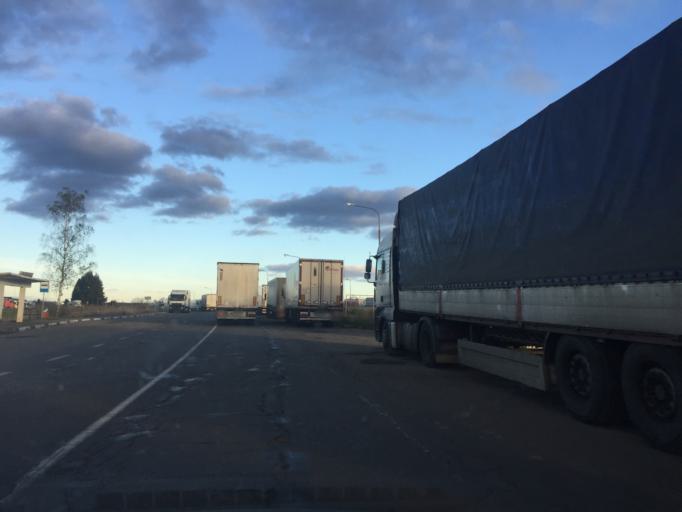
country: BY
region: Vitebsk
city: Myory
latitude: 55.8157
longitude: 27.6670
